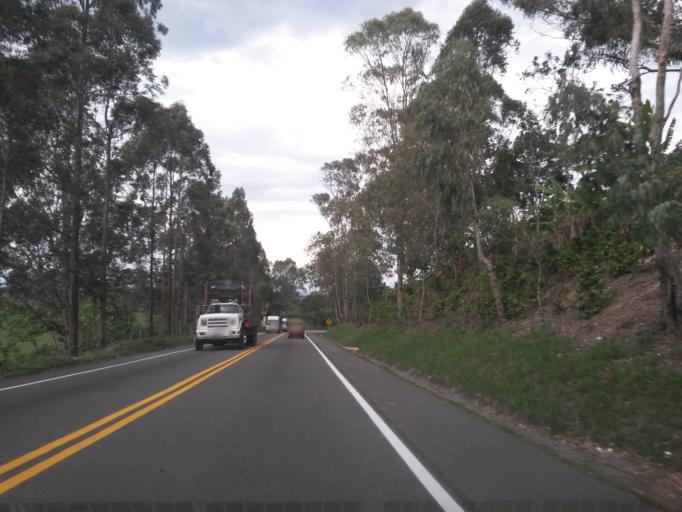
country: CO
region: Cauca
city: Popayan
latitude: 2.3718
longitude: -76.6786
